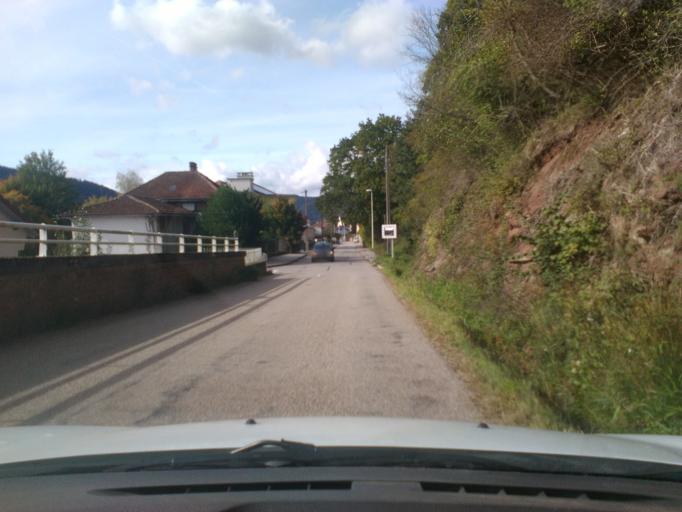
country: FR
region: Lorraine
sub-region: Departement des Vosges
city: Saint-Die-des-Vosges
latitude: 48.2871
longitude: 6.9622
